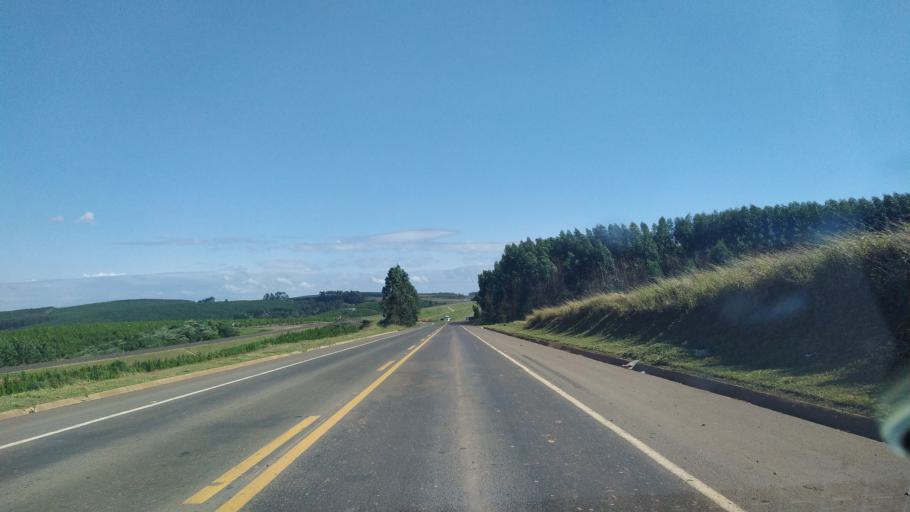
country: BR
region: Parana
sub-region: Telemaco Borba
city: Telemaco Borba
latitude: -24.2392
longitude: -50.7635
